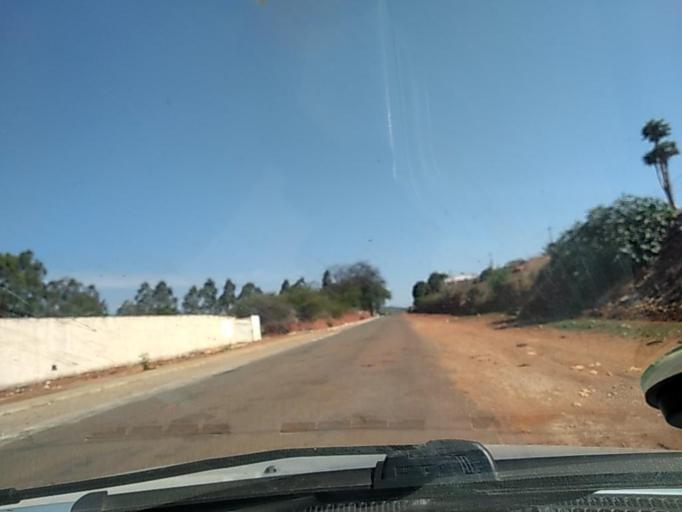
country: BR
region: Bahia
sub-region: Caetite
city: Caetite
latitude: -14.0507
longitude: -42.4849
